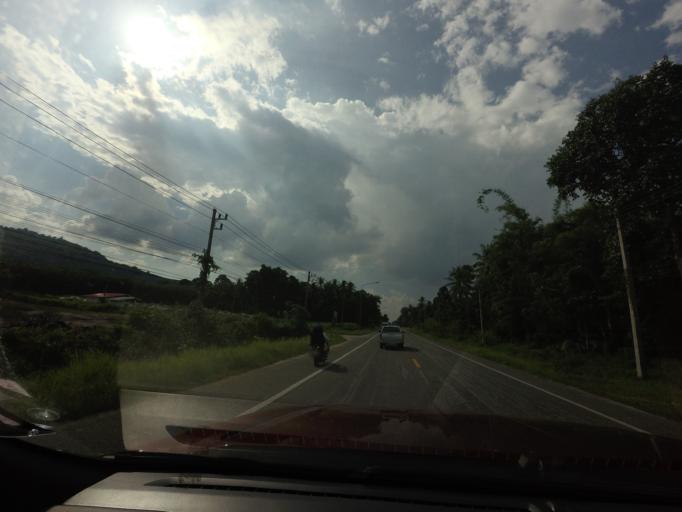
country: TH
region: Pattani
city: Mae Lan
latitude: 6.5918
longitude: 101.1957
